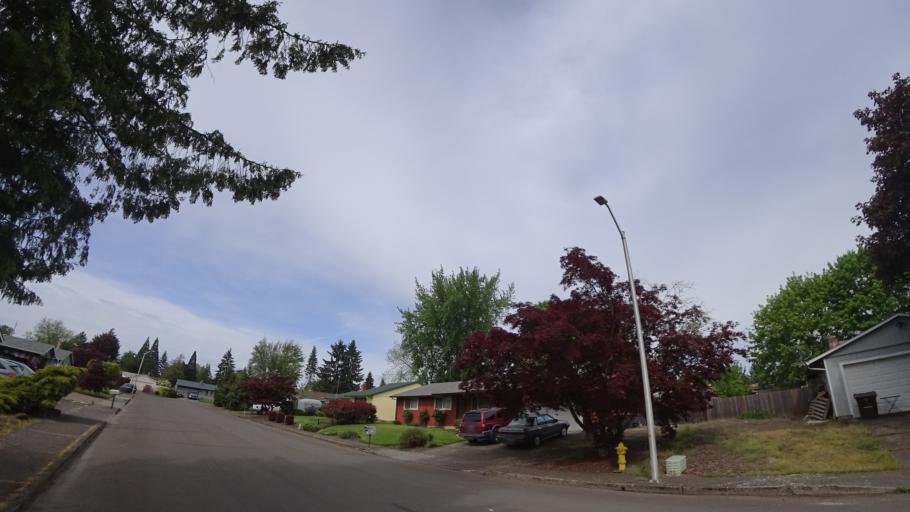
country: US
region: Oregon
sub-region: Washington County
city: Hillsboro
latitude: 45.5177
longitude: -122.9458
